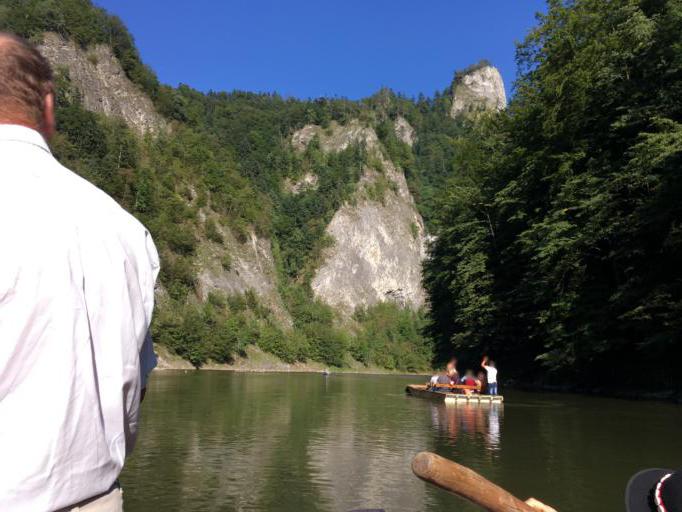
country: PL
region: Lesser Poland Voivodeship
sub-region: Powiat nowotarski
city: Kroscienko nad Dunajcem
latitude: 49.4176
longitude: 20.4323
